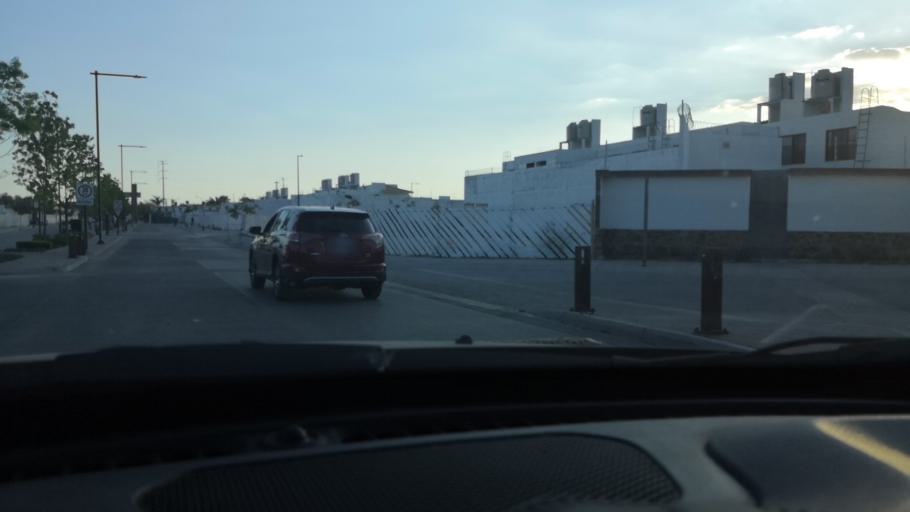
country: MX
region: Guanajuato
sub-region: Leon
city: San Jose de Duran (Los Troncoso)
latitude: 21.0854
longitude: -101.6537
